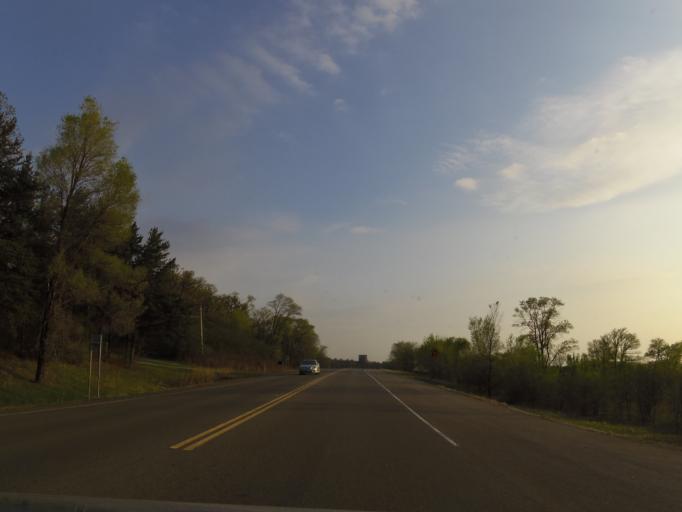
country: US
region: Minnesota
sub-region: Dakota County
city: Eagan
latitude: 44.8384
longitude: -93.1883
